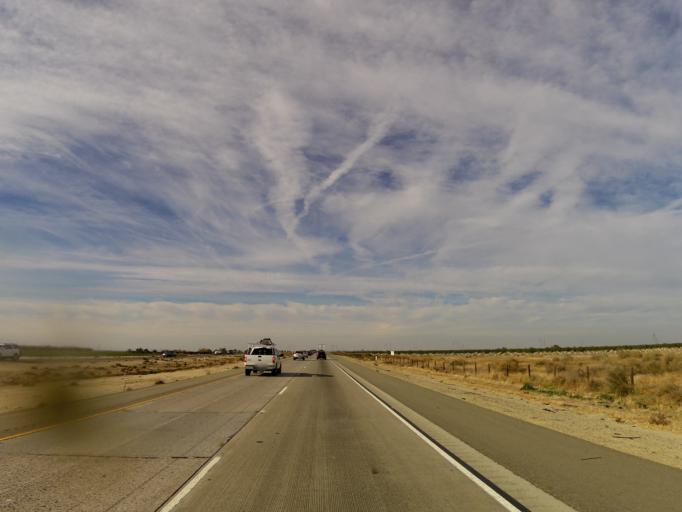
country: US
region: California
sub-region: Kern County
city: Buttonwillow
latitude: 35.3684
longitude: -119.3545
